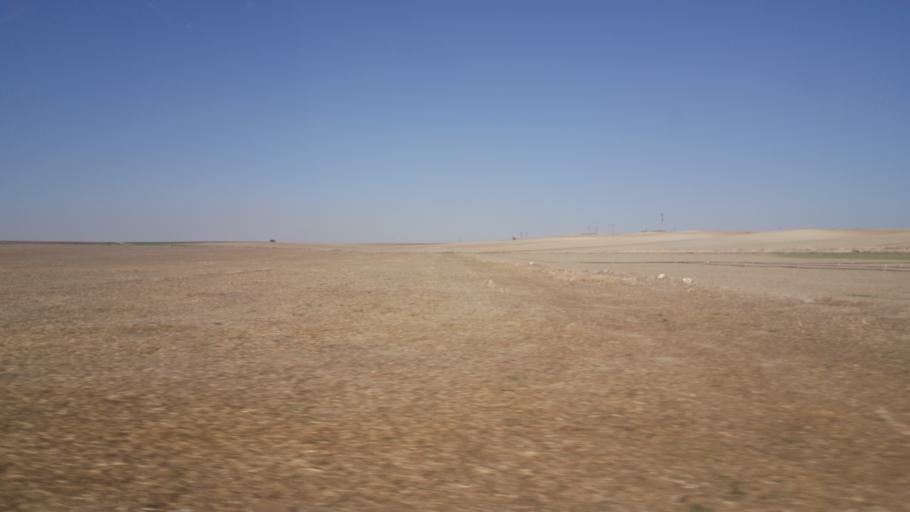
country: TR
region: Konya
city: Celtik
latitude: 39.0636
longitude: 31.8828
